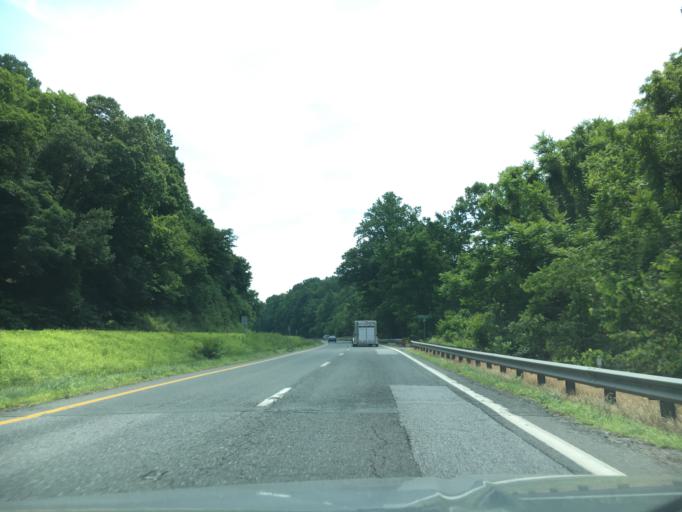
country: US
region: Virginia
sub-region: Campbell County
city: Concord
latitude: 37.3759
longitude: -79.0417
